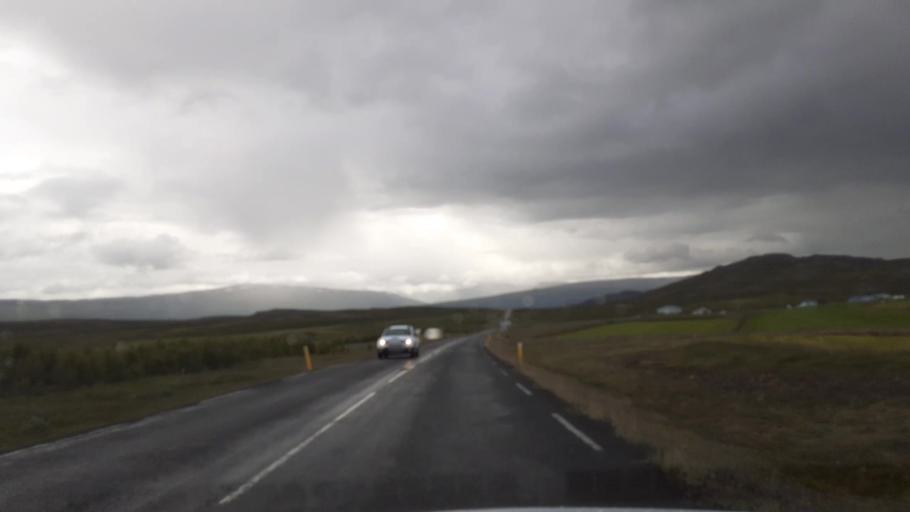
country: IS
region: East
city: Egilsstadir
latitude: 65.3333
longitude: -14.4862
